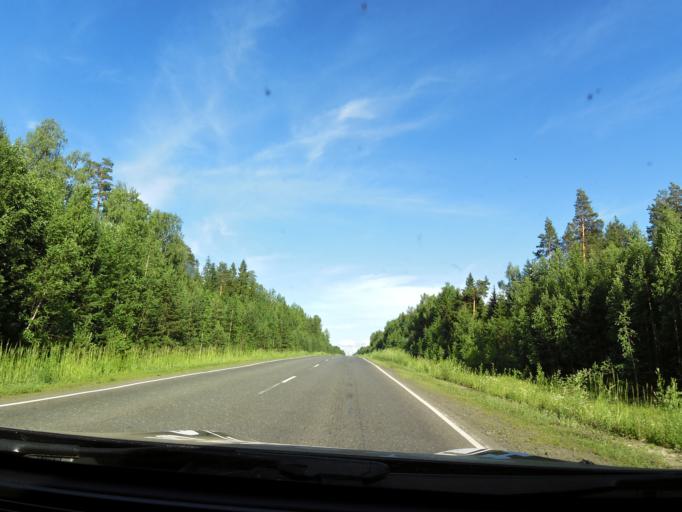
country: RU
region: Kirov
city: Chernaya Kholunitsa
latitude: 58.8859
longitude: 51.3930
